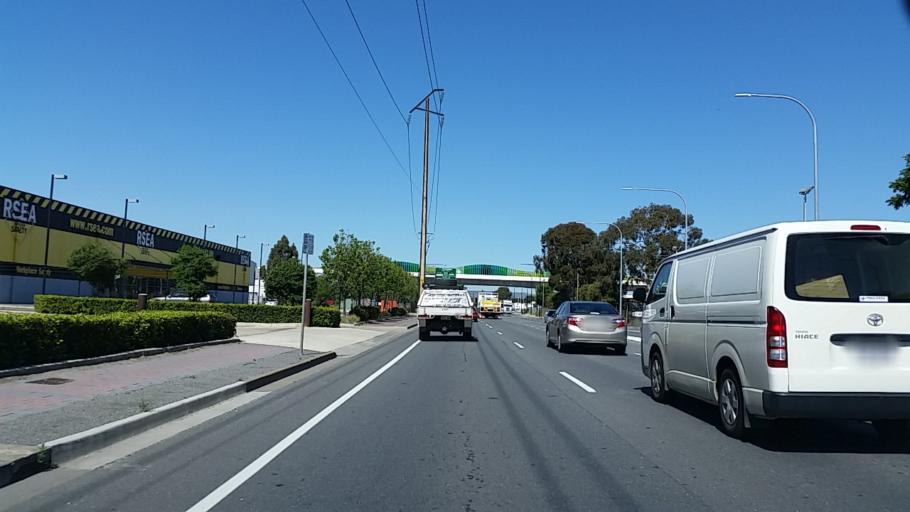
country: AU
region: South Australia
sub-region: Charles Sturt
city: Woodville North
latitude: -34.8499
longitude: 138.5605
